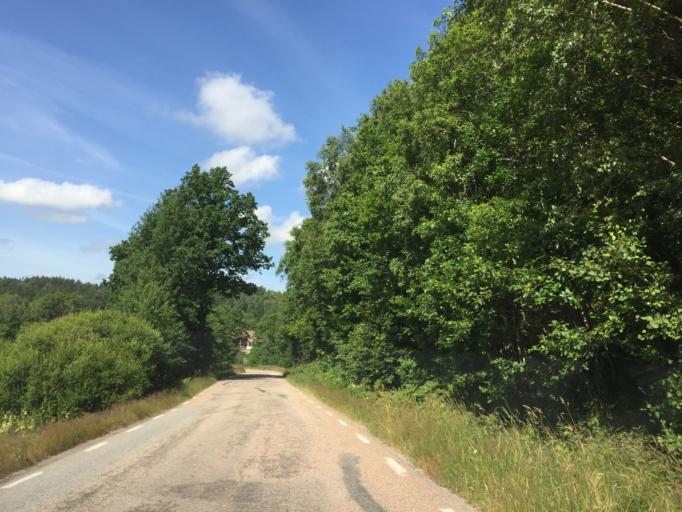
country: SE
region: Vaestra Goetaland
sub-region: Orust
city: Henan
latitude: 58.2923
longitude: 11.6389
